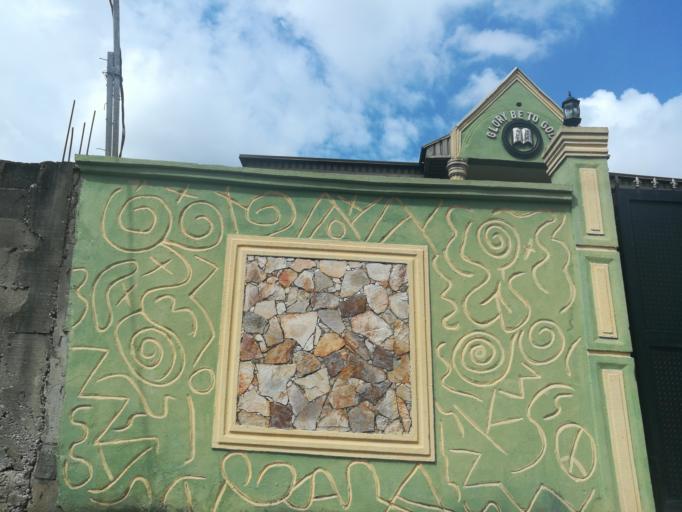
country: NG
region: Lagos
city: Somolu
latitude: 6.5491
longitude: 3.3735
